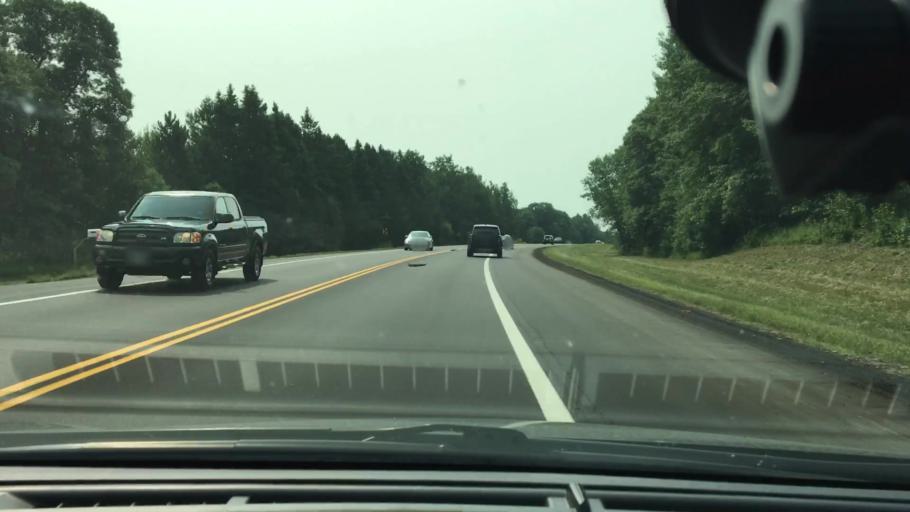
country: US
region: Minnesota
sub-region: Crow Wing County
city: Brainerd
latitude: 46.4124
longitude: -94.1763
